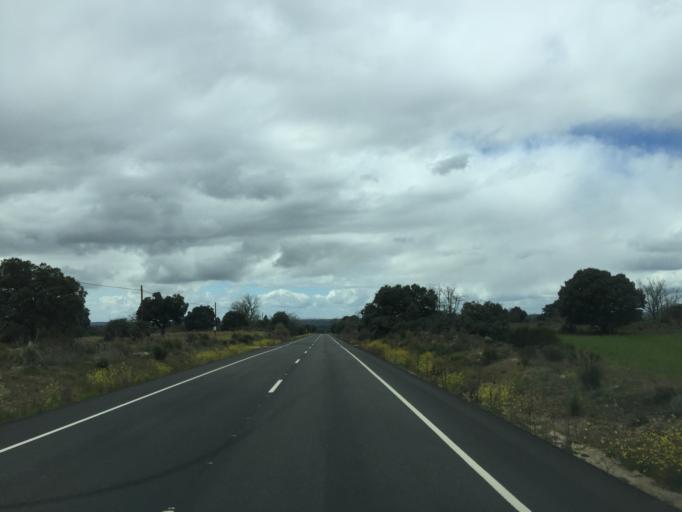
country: ES
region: Castille and Leon
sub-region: Provincia de Zamora
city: Arganin
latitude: 41.4752
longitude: -6.2265
